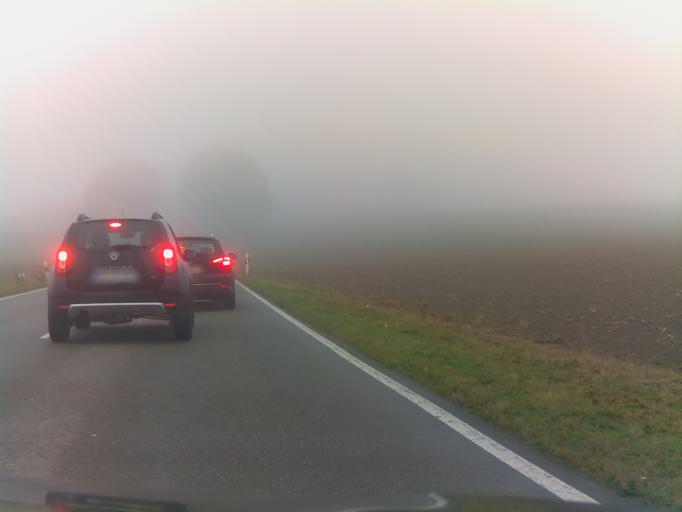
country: DE
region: Baden-Wuerttemberg
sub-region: Karlsruhe Region
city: Olbronn-Durrn
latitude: 48.9745
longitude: 8.7286
